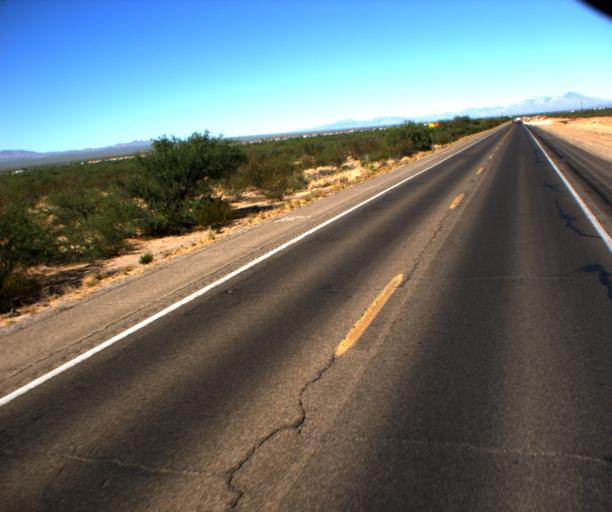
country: US
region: Arizona
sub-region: Pima County
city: Valencia West
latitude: 32.1507
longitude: -111.1243
